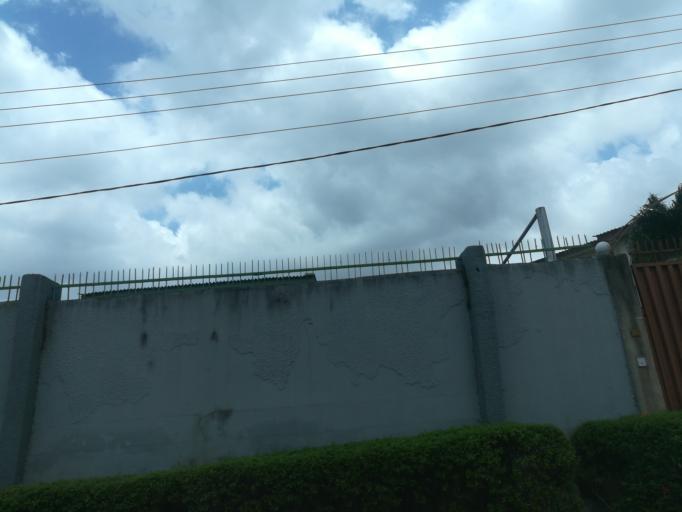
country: NG
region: Lagos
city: Somolu
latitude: 6.5559
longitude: 3.3655
